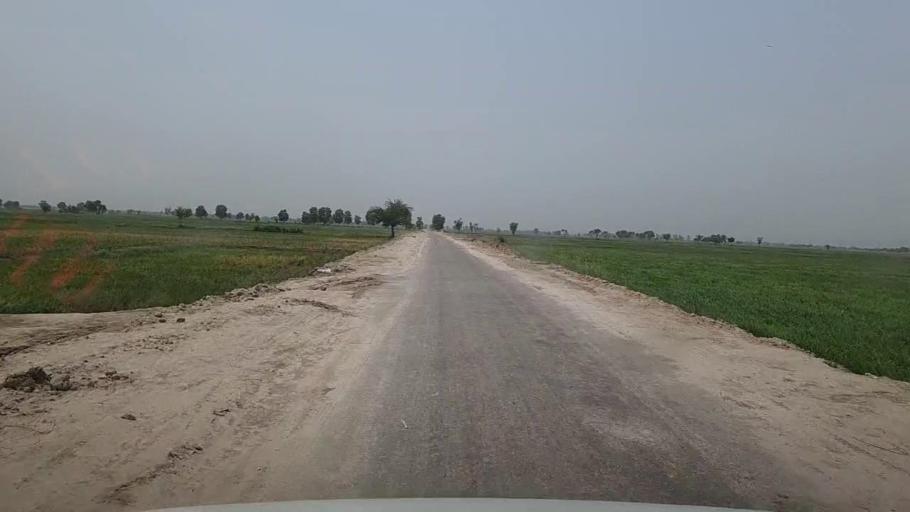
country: PK
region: Sindh
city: Sita Road
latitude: 27.0876
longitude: 67.9129
